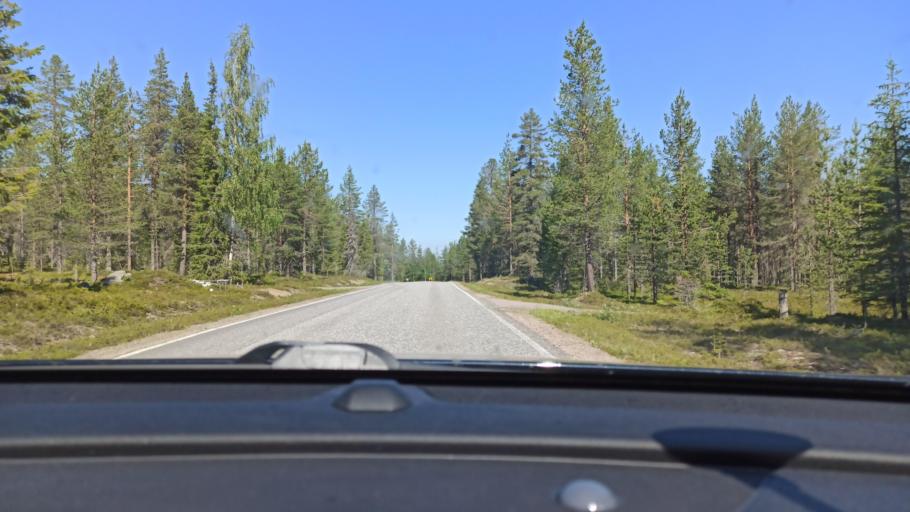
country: FI
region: Lapland
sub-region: Tunturi-Lappi
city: Kolari
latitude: 67.6804
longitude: 24.1386
